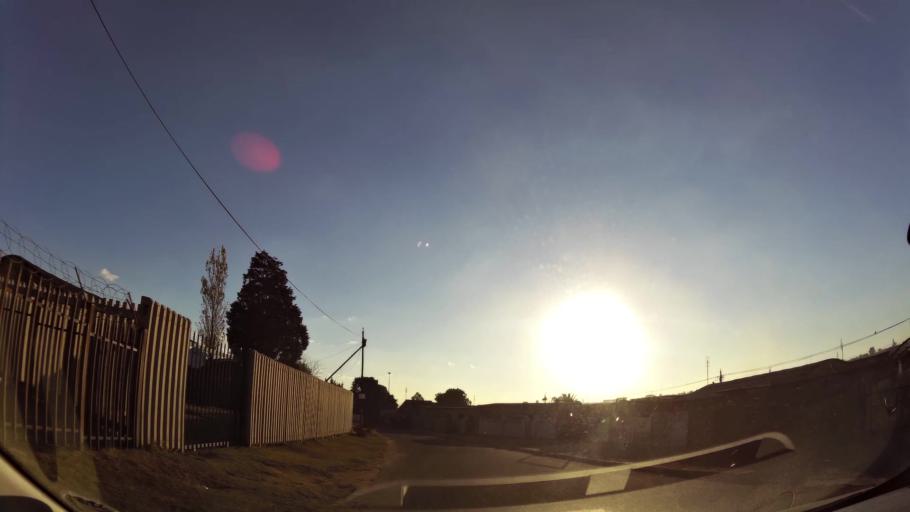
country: ZA
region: Mpumalanga
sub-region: Nkangala District Municipality
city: Witbank
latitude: -25.8772
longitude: 29.1899
